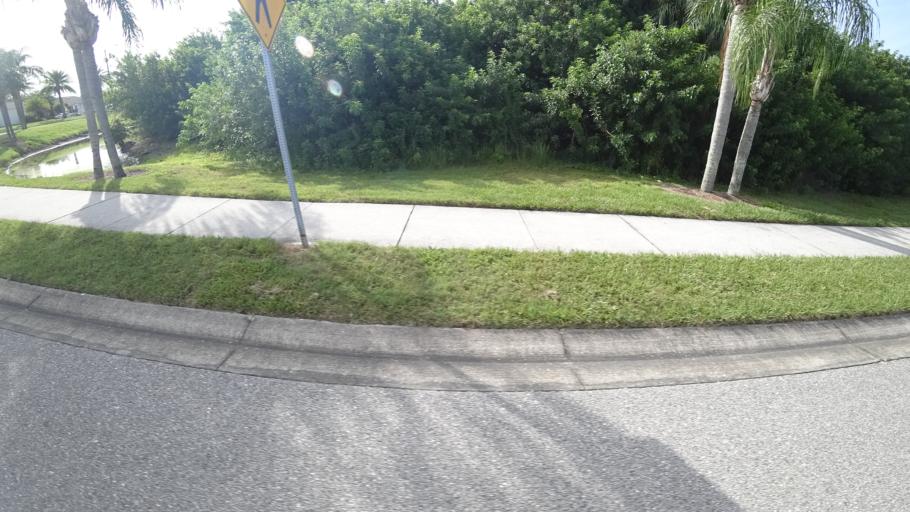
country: US
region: Florida
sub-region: Manatee County
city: Ellenton
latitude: 27.5538
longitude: -82.5014
